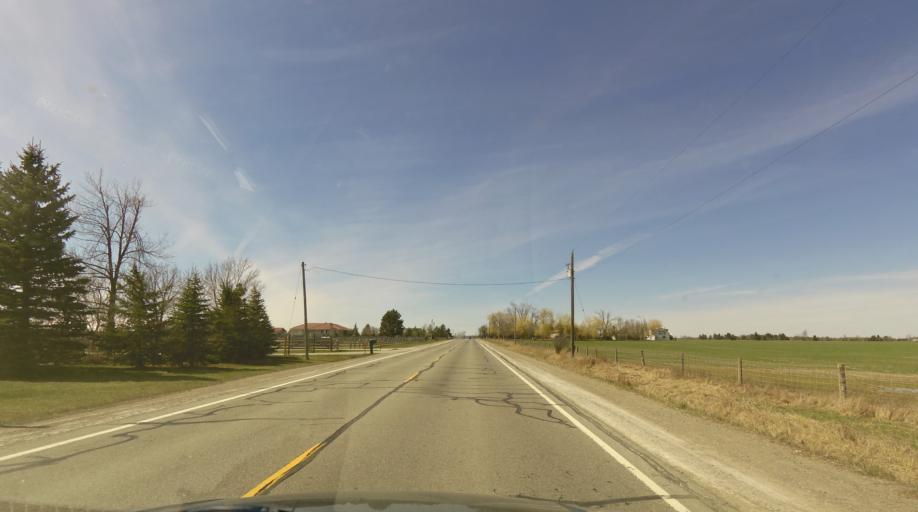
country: CA
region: Ontario
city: Brampton
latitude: 43.7081
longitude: -79.8853
